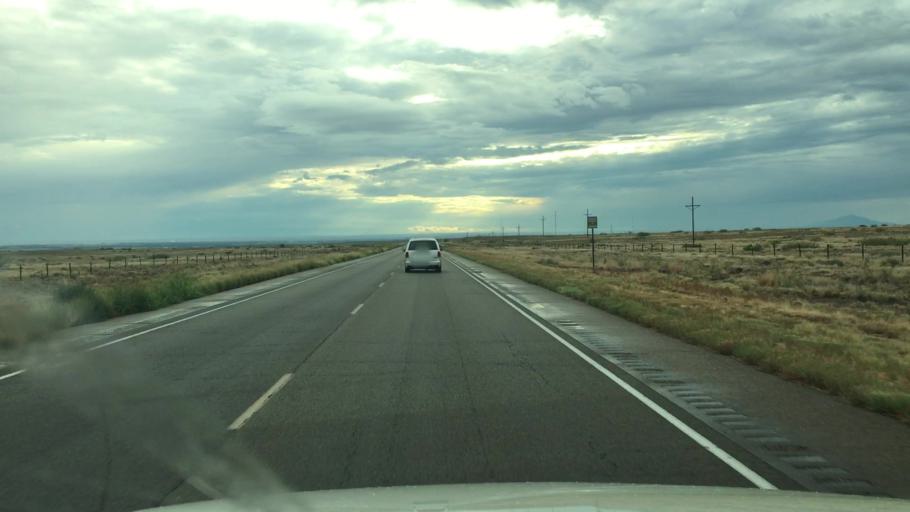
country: US
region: New Mexico
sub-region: Chaves County
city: Roswell
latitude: 33.4008
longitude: -104.3374
